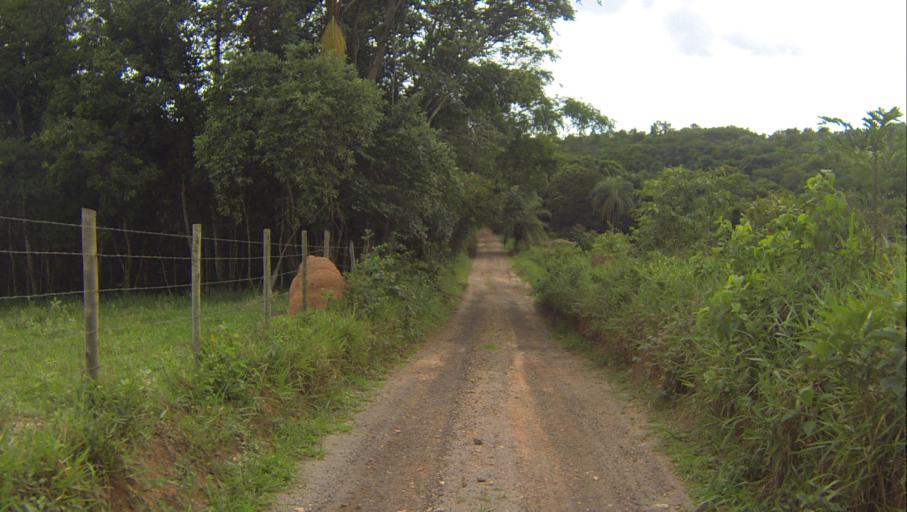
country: BR
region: Minas Gerais
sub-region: Brumadinho
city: Brumadinho
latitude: -20.1650
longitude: -44.1288
